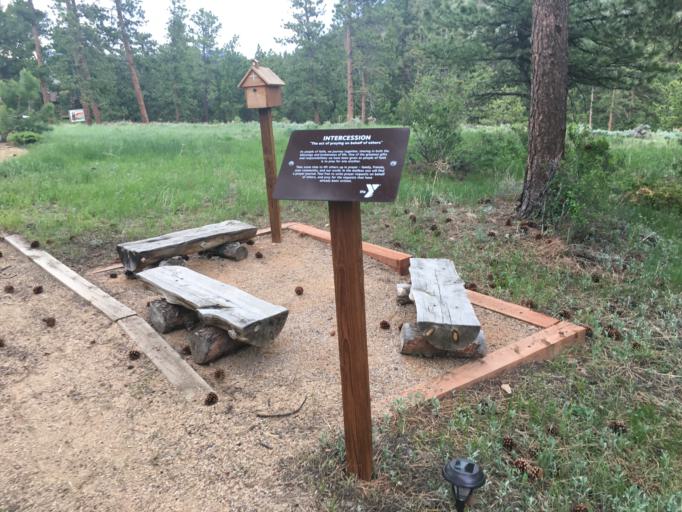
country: US
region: Colorado
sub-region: Larimer County
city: Estes Park
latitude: 40.3417
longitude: -105.5694
